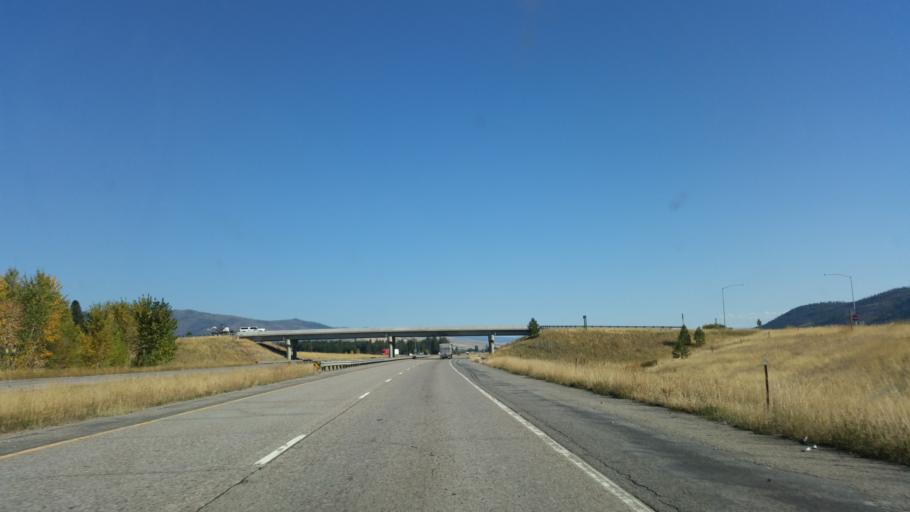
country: US
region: Montana
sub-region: Missoula County
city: Frenchtown
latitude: 47.0332
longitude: -114.3258
